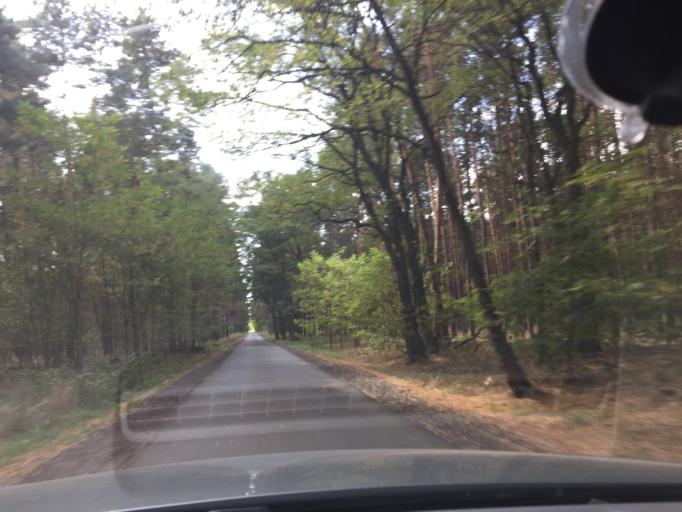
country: DE
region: Brandenburg
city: Spreenhagen
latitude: 52.3690
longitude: 13.8865
